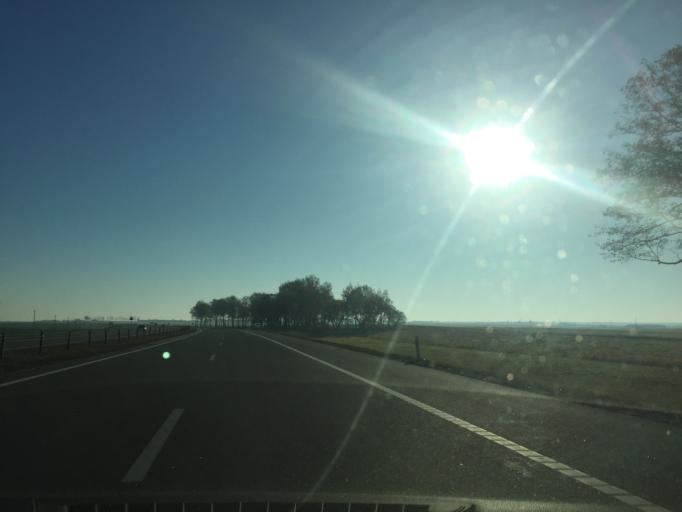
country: BY
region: Minsk
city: Luhavaya Slabada
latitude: 53.7622
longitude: 27.8784
